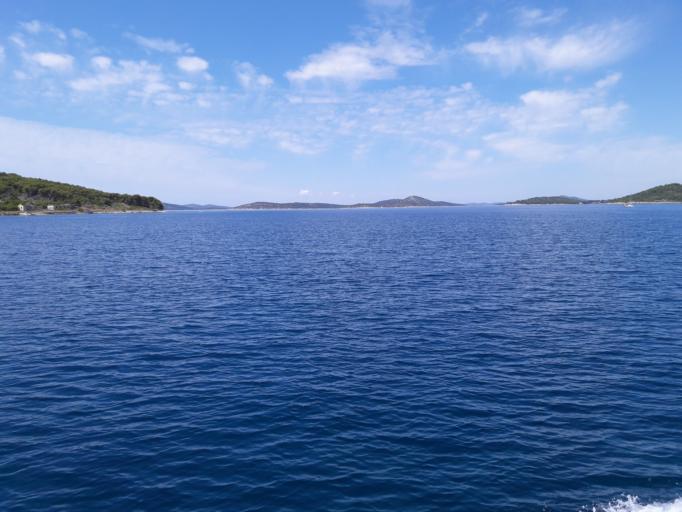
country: HR
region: Sibensko-Kniniska
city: Vodice
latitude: 43.7015
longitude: 15.8308
